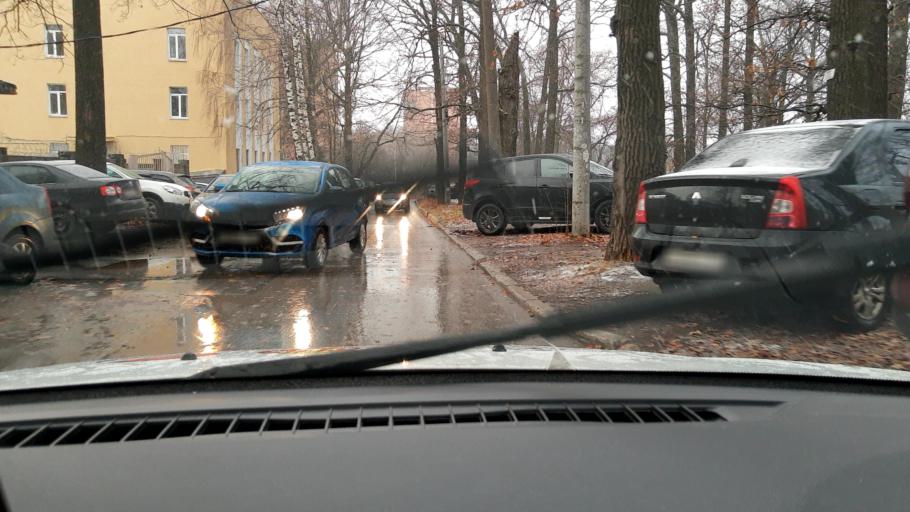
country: RU
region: Nizjnij Novgorod
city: Nizhniy Novgorod
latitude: 56.2572
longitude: 43.9739
